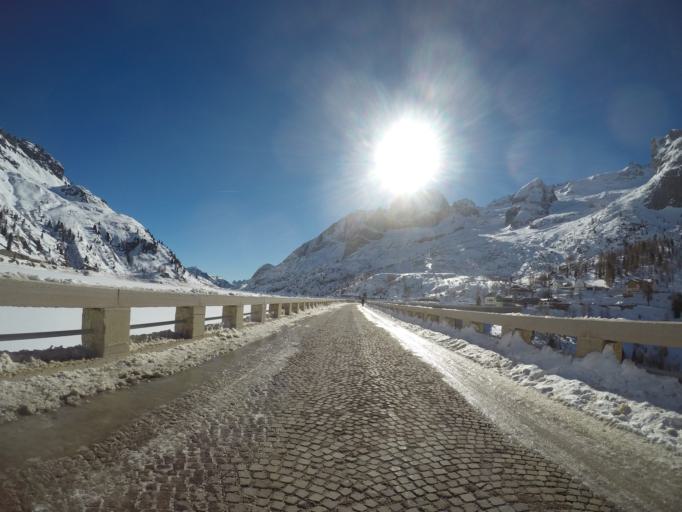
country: IT
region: Trentino-Alto Adige
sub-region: Bolzano
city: Corvara in Badia
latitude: 46.4616
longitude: 11.8634
